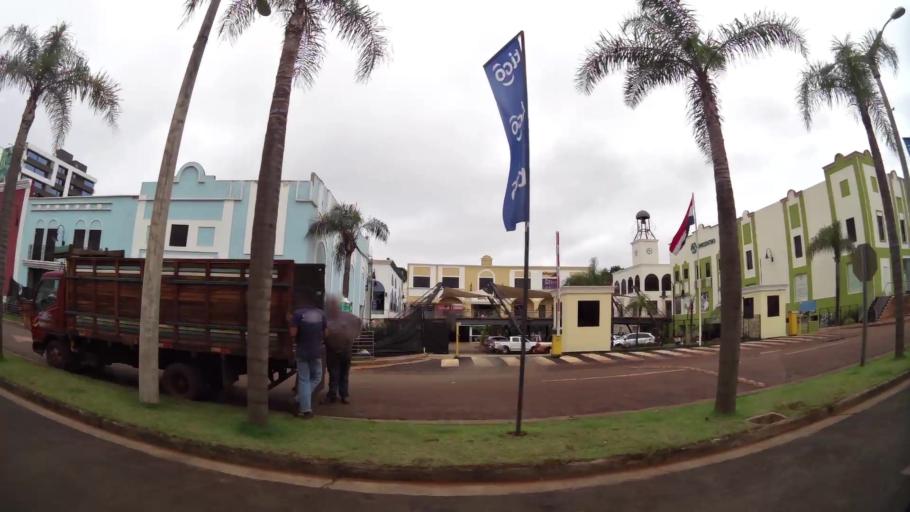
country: PY
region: Alto Parana
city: Ciudad del Este
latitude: -25.4977
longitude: -54.6794
